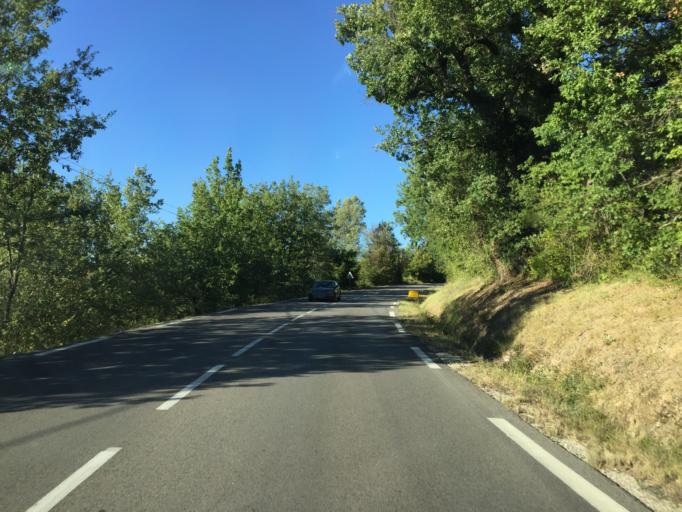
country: FR
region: Provence-Alpes-Cote d'Azur
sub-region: Departement des Alpes-de-Haute-Provence
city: Cereste
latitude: 43.8571
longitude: 5.5649
